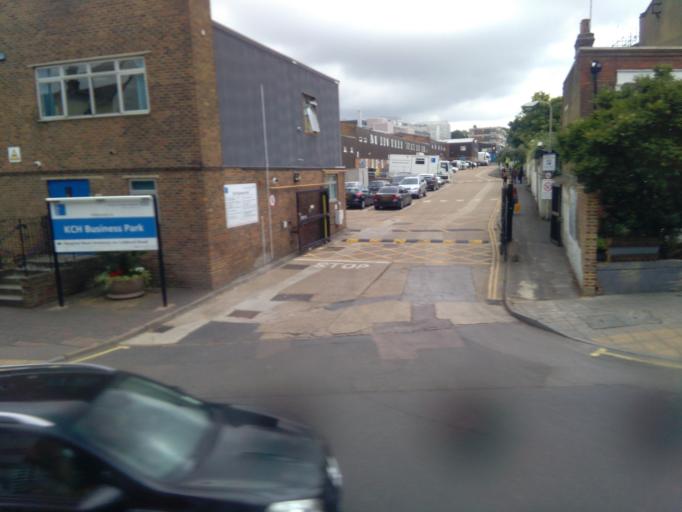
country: GB
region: England
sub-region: Greater London
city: Camberwell
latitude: 51.4688
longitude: -0.0981
